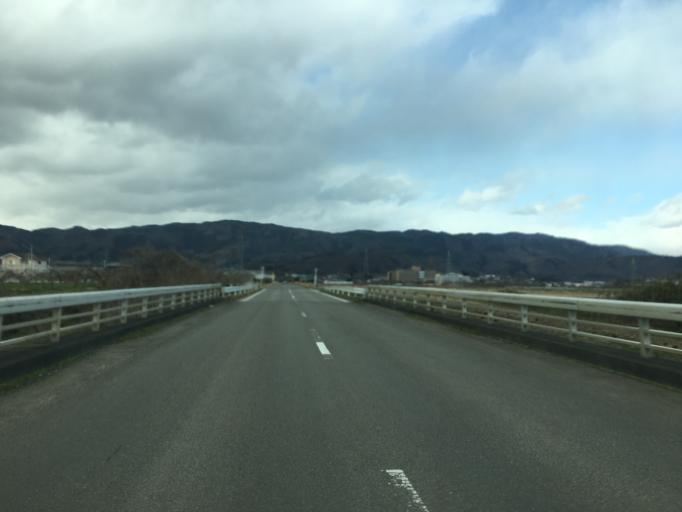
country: JP
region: Fukushima
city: Hobaramachi
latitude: 37.8629
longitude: 140.5379
